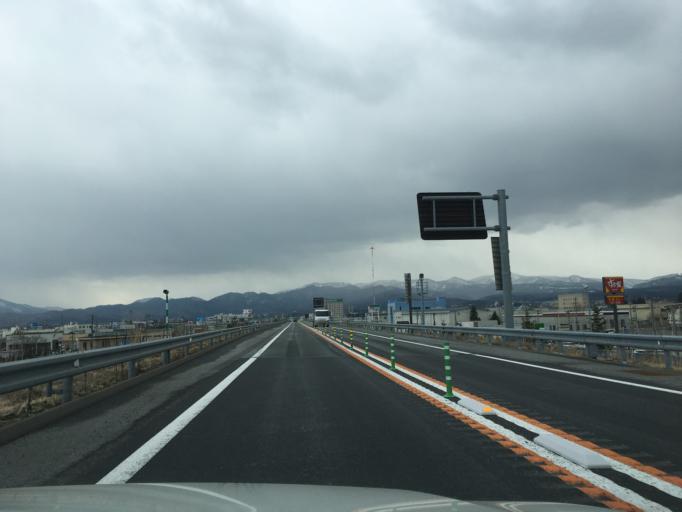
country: JP
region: Aomori
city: Aomori Shi
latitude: 40.7958
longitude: 140.7478
